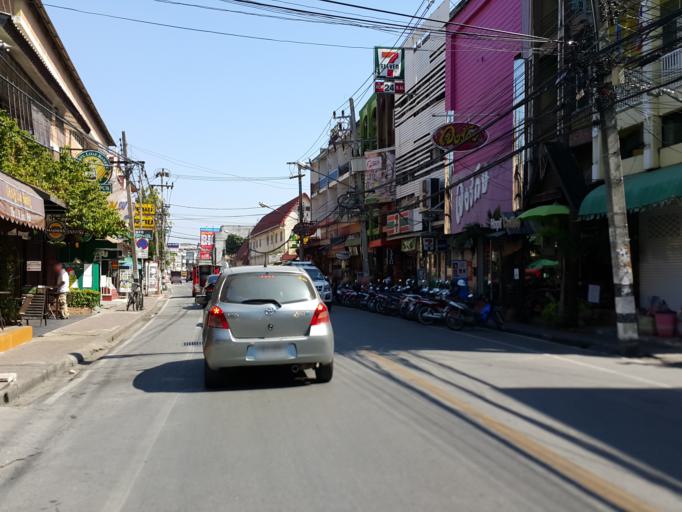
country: TH
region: Chiang Mai
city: Chiang Mai
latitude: 18.7906
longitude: 98.9913
